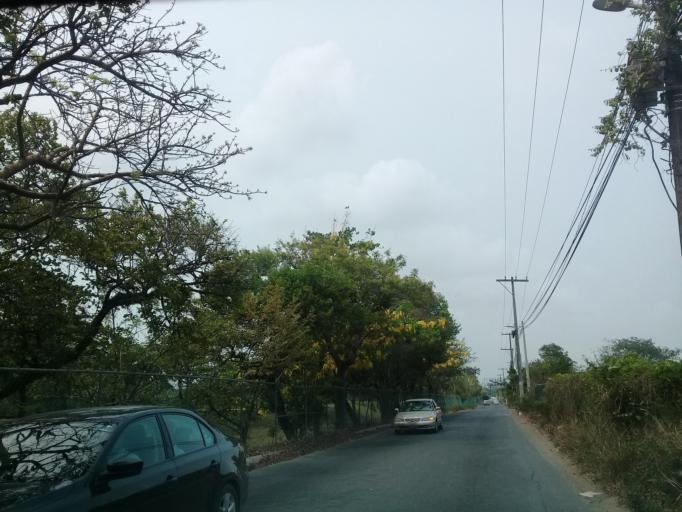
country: MX
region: Veracruz
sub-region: Veracruz
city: Hacienda Sotavento
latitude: 19.1420
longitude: -96.1770
